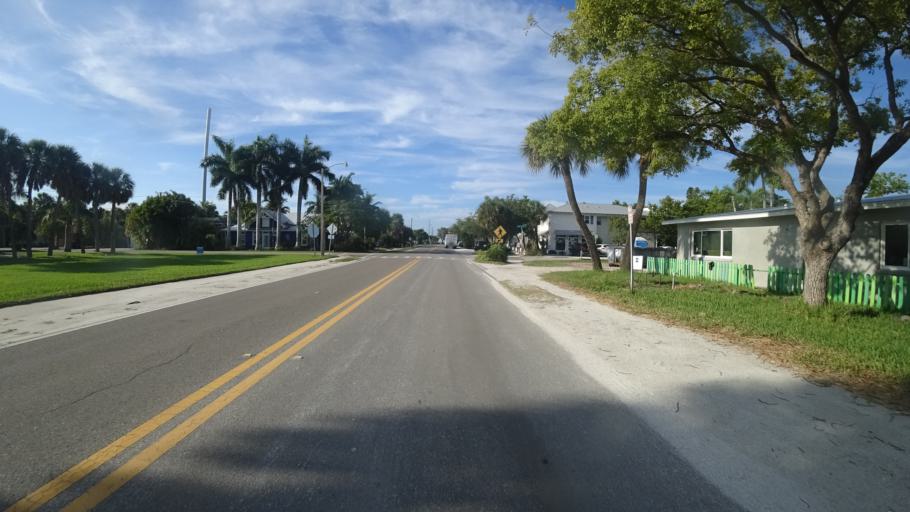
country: US
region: Florida
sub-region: Manatee County
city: Anna Maria
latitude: 27.5284
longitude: -82.7356
